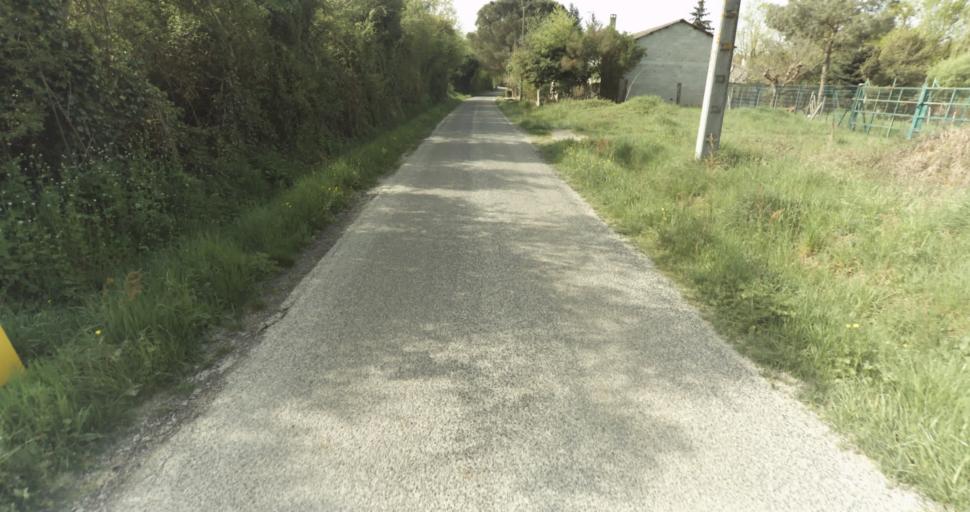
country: FR
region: Midi-Pyrenees
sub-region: Departement du Tarn-et-Garonne
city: Moissac
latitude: 44.0761
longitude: 1.0903
